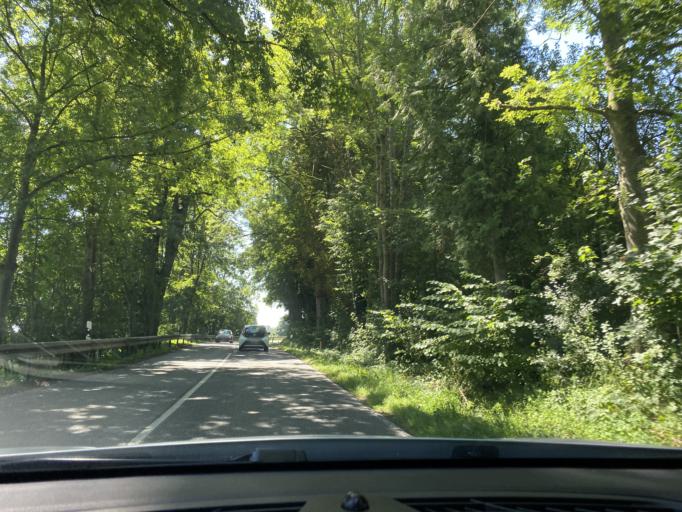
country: DE
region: Bavaria
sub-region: Upper Bavaria
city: Worth
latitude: 48.2718
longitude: 11.8903
